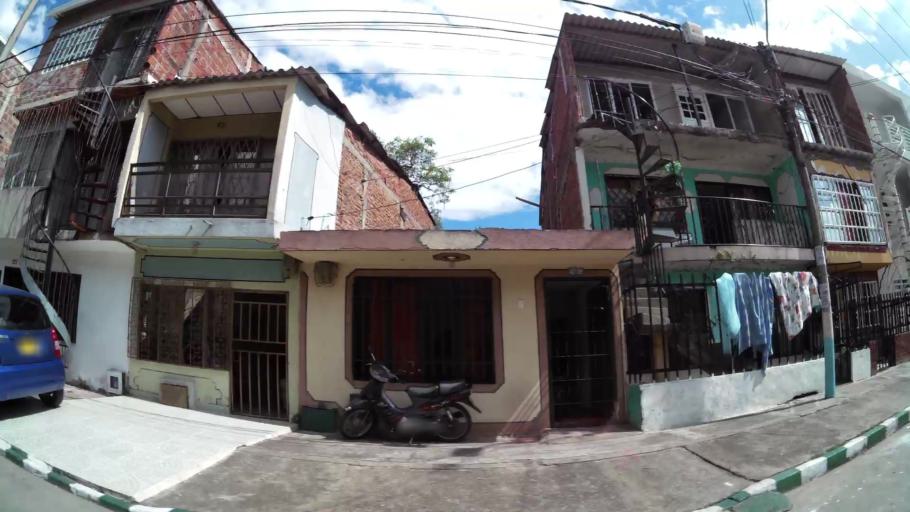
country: CO
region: Valle del Cauca
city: Cali
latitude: 3.4000
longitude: -76.5139
